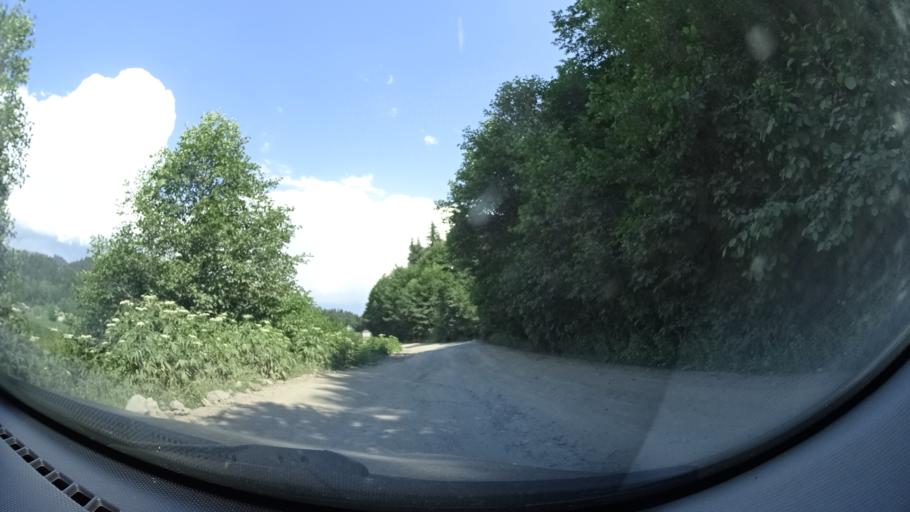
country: GE
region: Ajaria
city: Dioknisi
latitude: 41.6518
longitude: 42.4642
